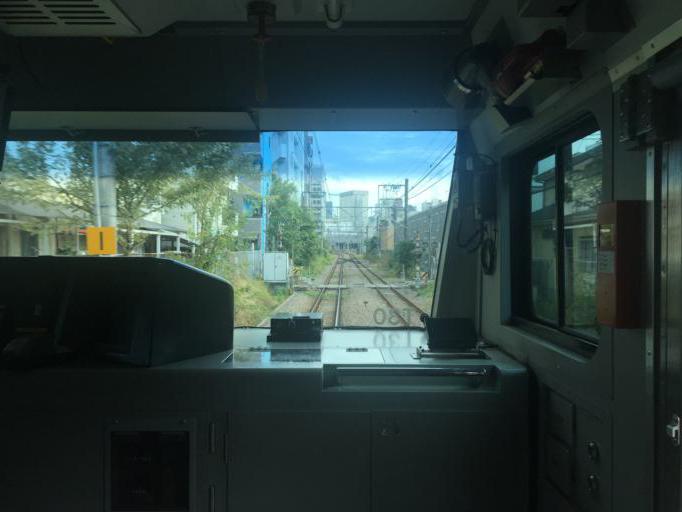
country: JP
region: Tokyo
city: Hino
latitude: 35.6991
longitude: 139.4080
